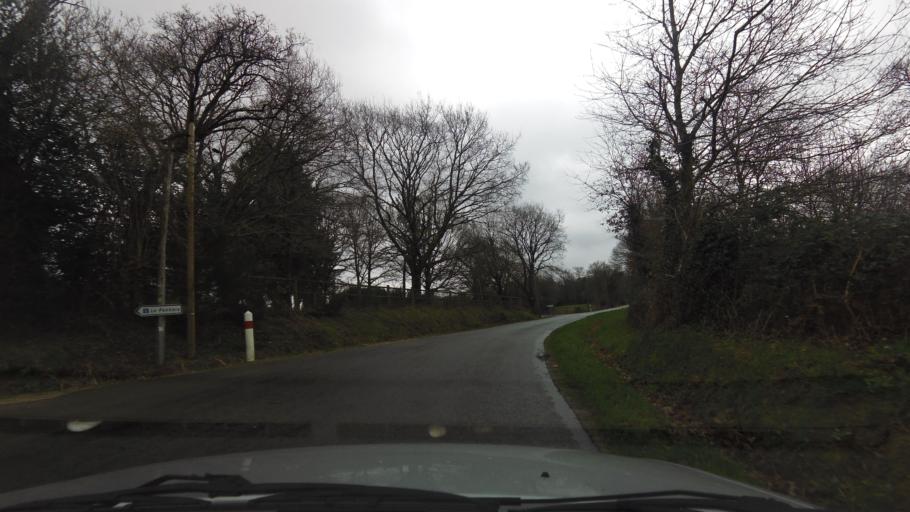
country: FR
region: Brittany
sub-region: Departement du Morbihan
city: Elven
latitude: 47.7870
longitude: -2.5640
